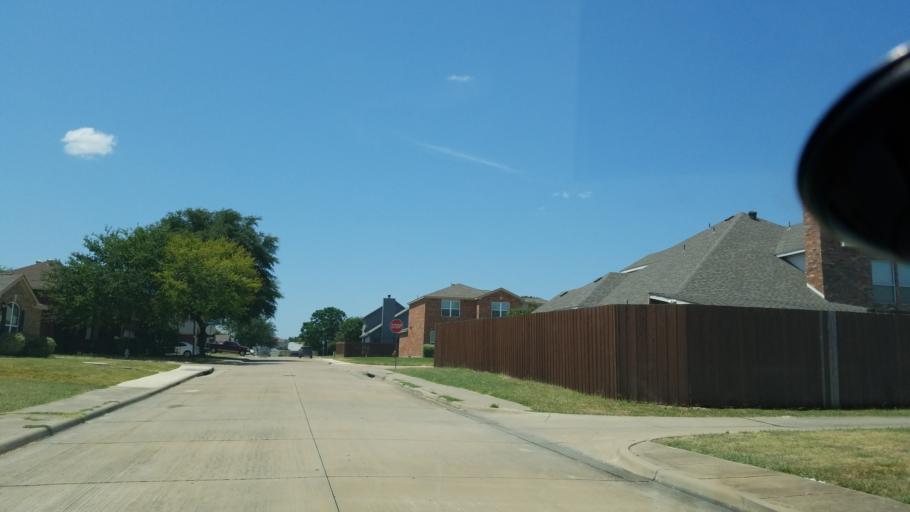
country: US
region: Texas
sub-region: Dallas County
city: Duncanville
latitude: 32.6400
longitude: -96.8852
